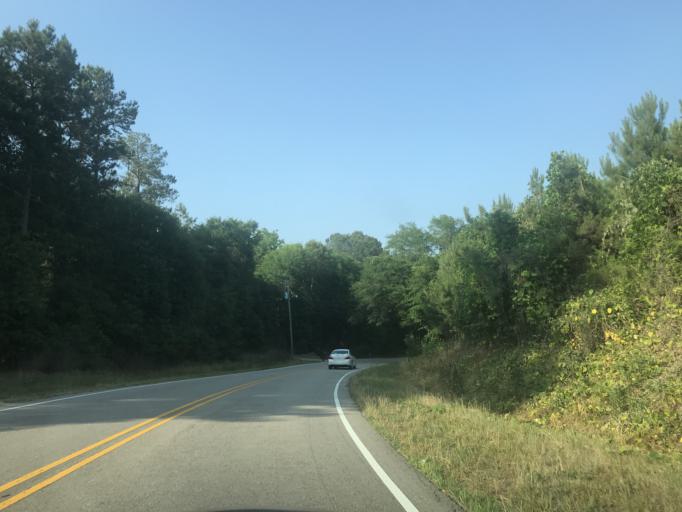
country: US
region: North Carolina
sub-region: Wake County
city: Knightdale
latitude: 35.8529
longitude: -78.5006
